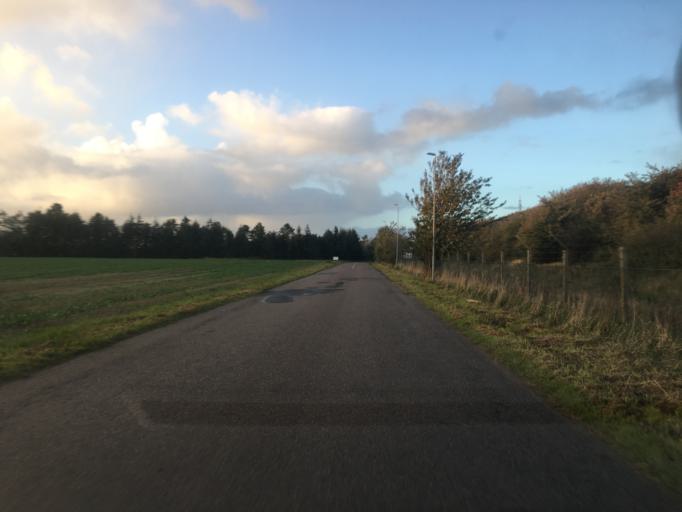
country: DK
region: South Denmark
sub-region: Tonder Kommune
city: Tonder
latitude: 54.9247
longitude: 8.8508
